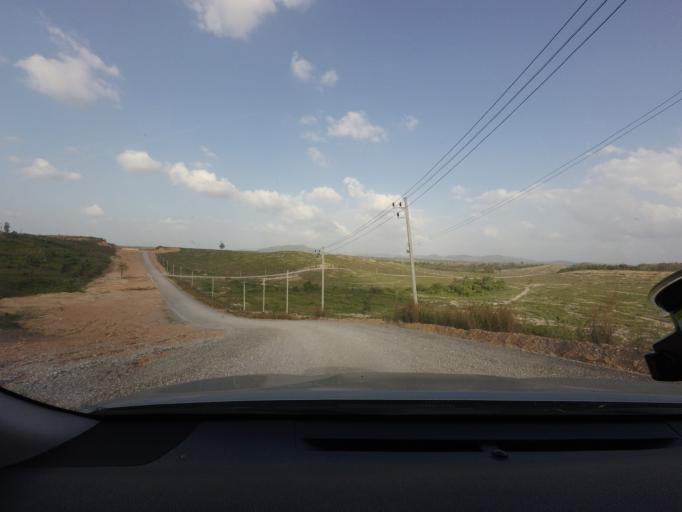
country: TH
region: Pattani
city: Mae Lan
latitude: 6.6045
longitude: 101.2497
